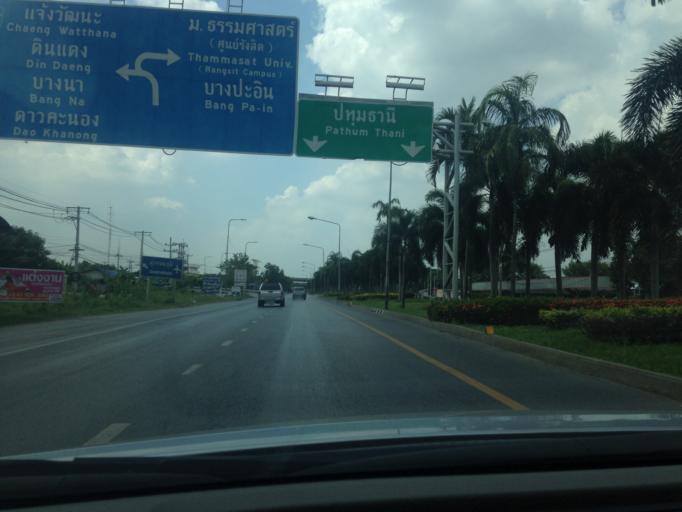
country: TH
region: Phra Nakhon Si Ayutthaya
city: Ban Bang Kadi Pathum Thani
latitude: 13.9977
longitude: 100.5734
